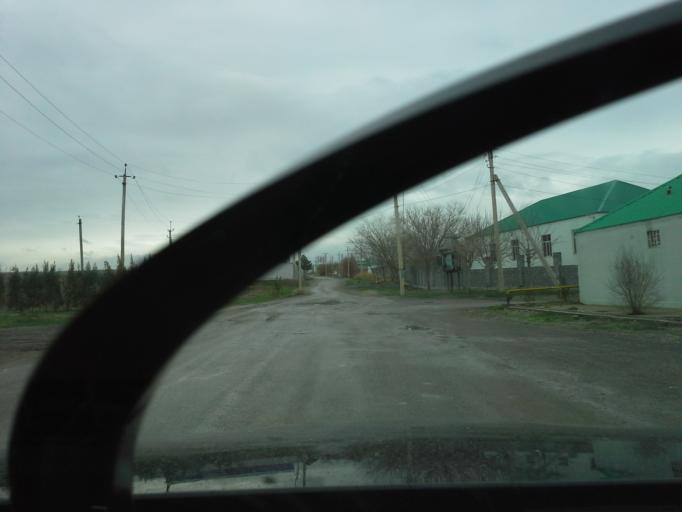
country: TM
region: Ahal
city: Abadan
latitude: 37.9654
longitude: 58.2293
